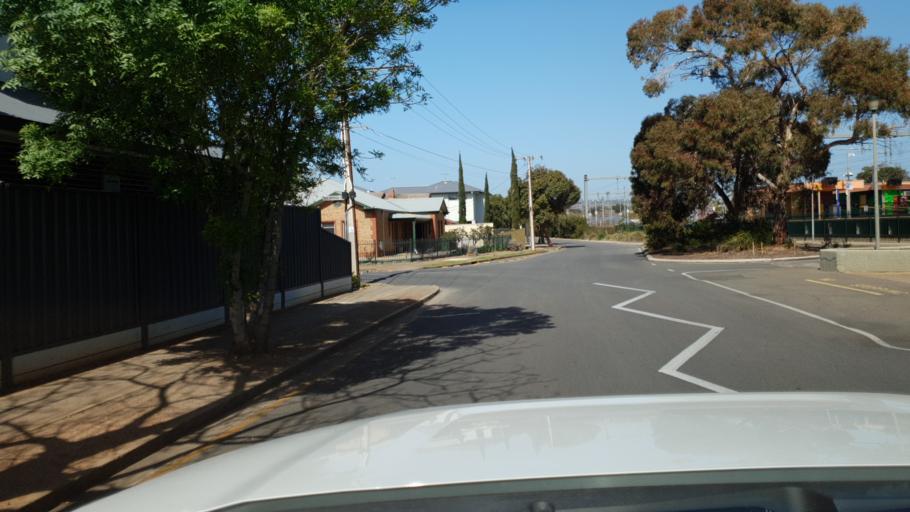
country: AU
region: South Australia
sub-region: Adelaide
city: Brighton
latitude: -35.0207
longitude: 138.5194
